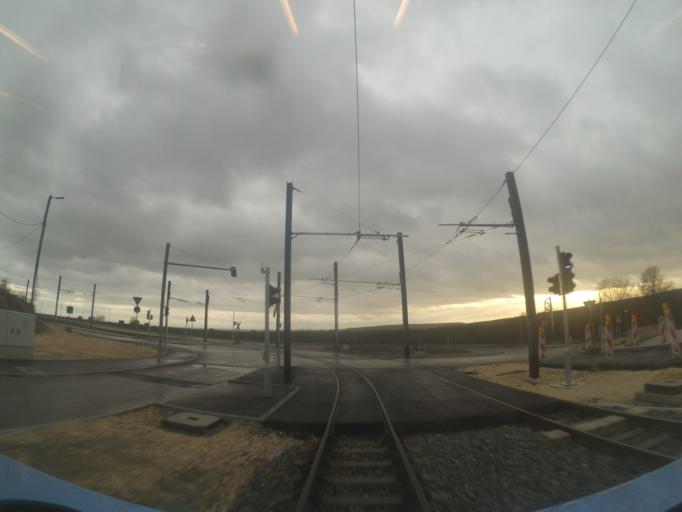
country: DE
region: Baden-Wuerttemberg
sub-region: Tuebingen Region
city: Dornstadt
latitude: 48.4191
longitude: 9.9356
